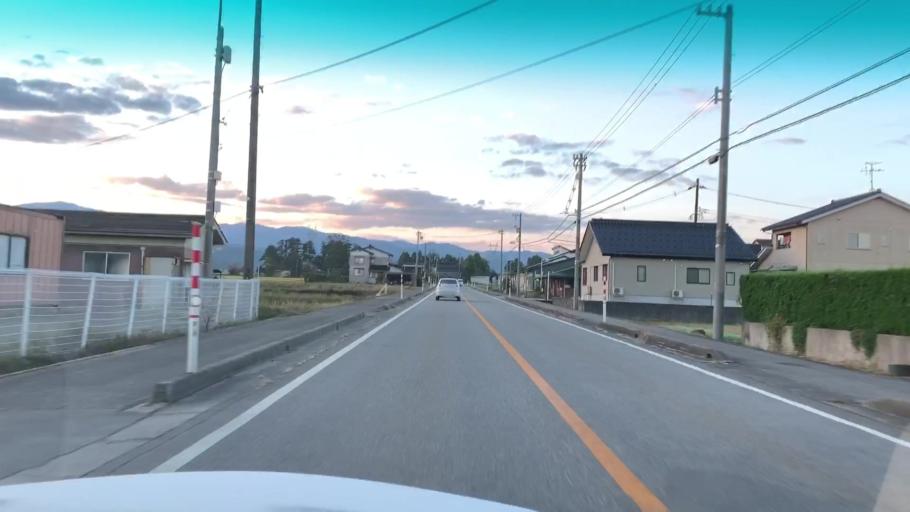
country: JP
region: Toyama
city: Kamiichi
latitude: 36.6662
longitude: 137.3276
